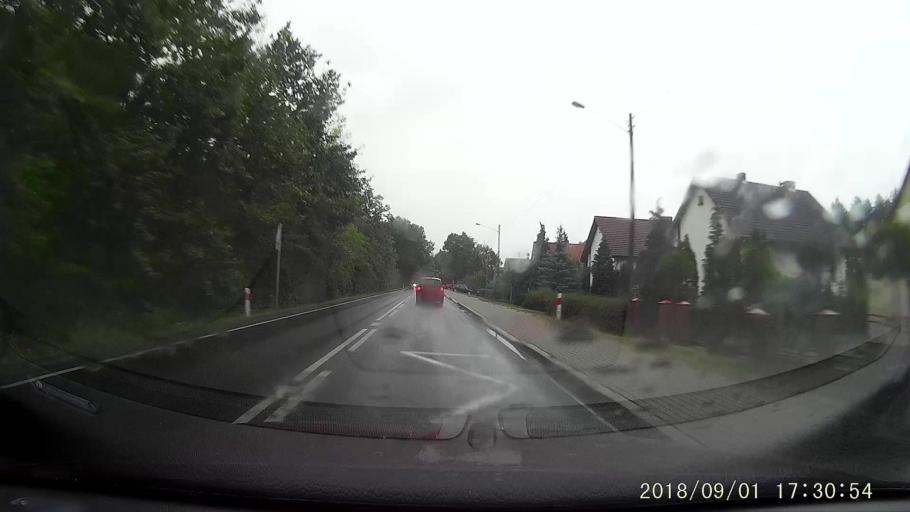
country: PL
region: Lubusz
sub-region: Powiat zaganski
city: Zagan
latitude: 51.6373
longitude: 15.3238
